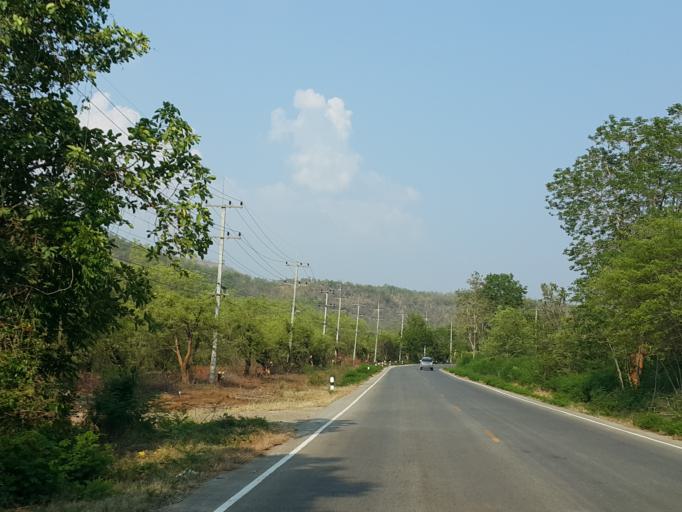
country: TH
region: Kanchanaburi
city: Sai Yok
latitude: 14.2204
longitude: 99.1618
